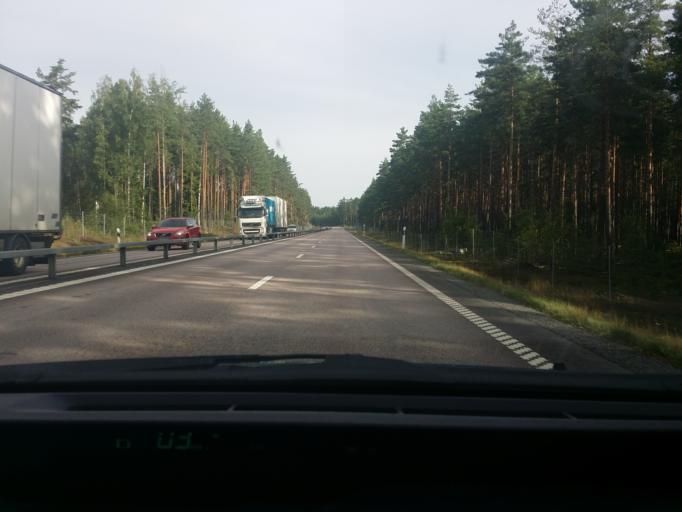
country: SE
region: Vaestmanland
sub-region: Sala Kommun
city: Sala
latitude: 59.8068
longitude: 16.5552
